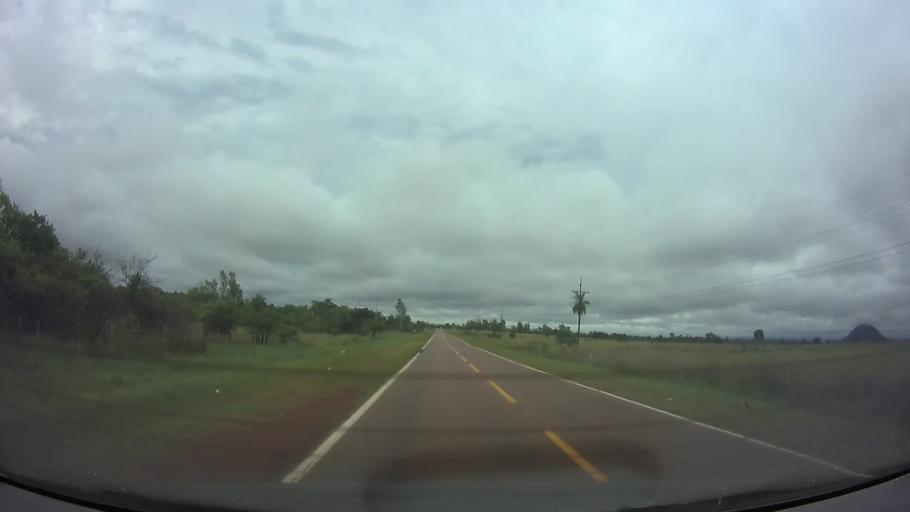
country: PY
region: Paraguari
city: Acahay
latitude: -25.8401
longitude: -57.1491
